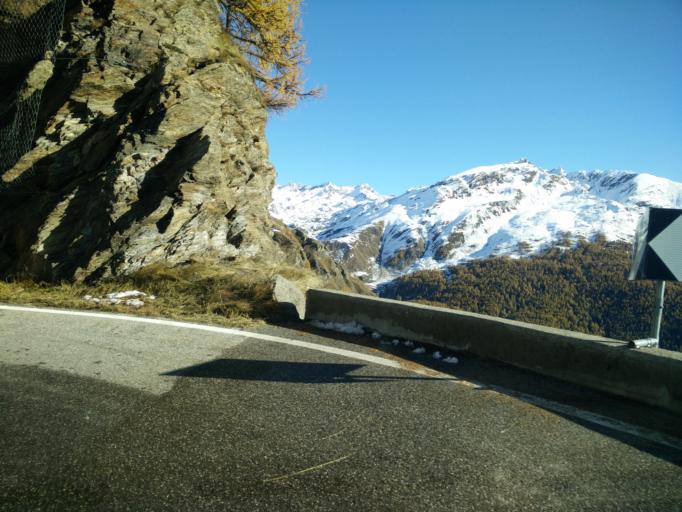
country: IT
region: Trentino-Alto Adige
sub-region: Bolzano
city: Moso in Passiria
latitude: 46.8821
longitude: 11.1154
